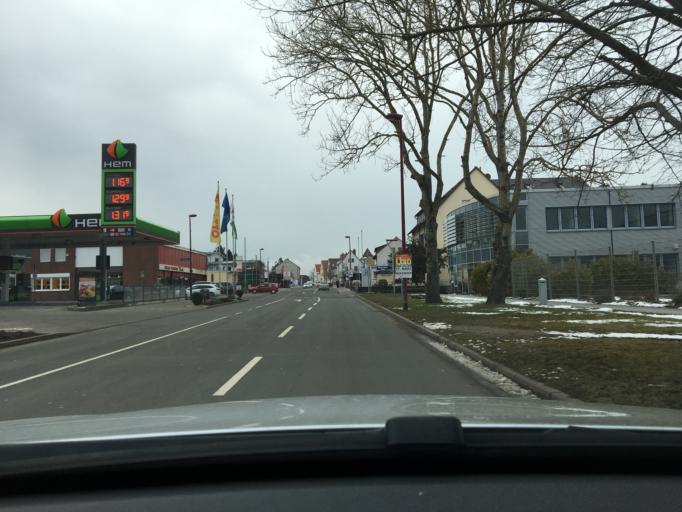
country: DE
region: Rheinland-Pfalz
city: Kirchheimbolanden
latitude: 49.6557
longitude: 8.0176
